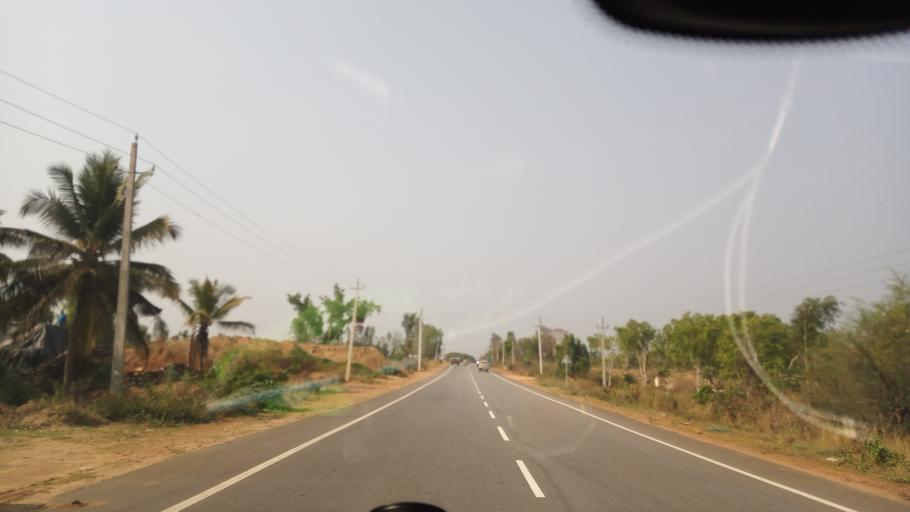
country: IN
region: Karnataka
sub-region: Mandya
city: Melukote
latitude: 12.6980
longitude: 76.6981
